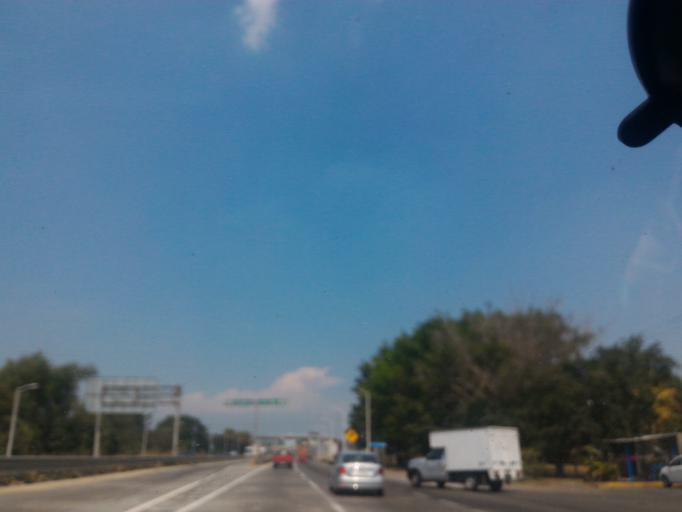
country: MX
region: Colima
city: Colima
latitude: 19.2092
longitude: -103.7413
